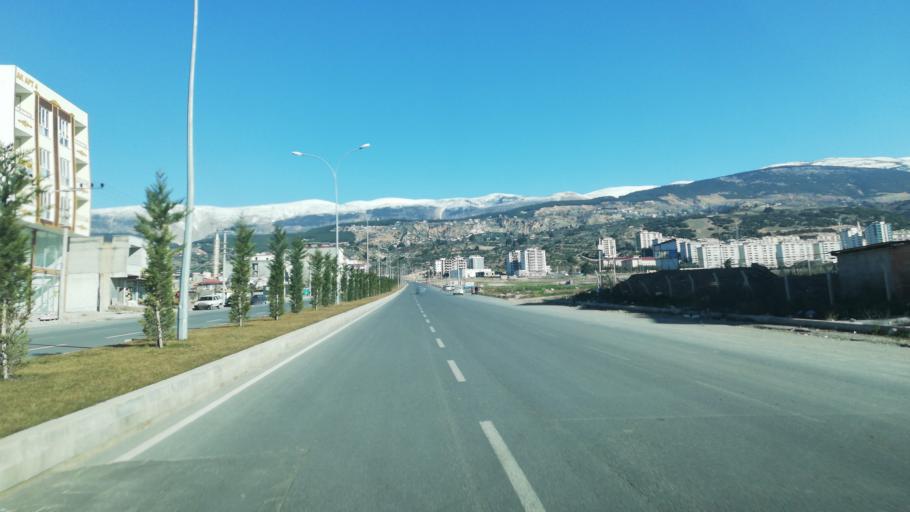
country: TR
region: Kahramanmaras
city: Kahramanmaras
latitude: 37.5762
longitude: 36.9746
